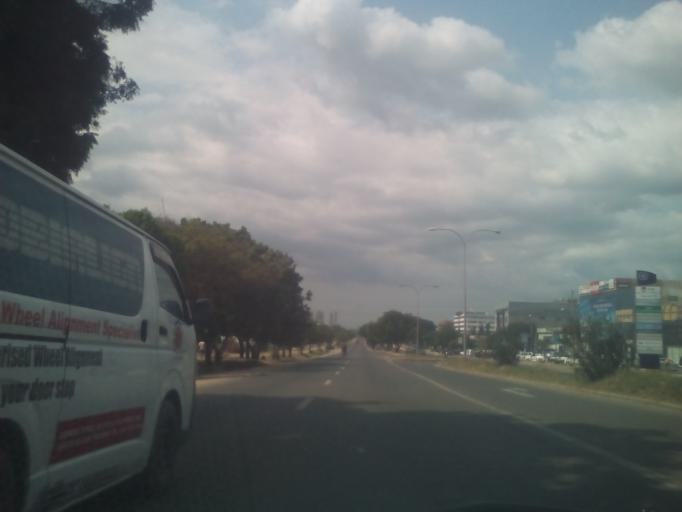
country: TZ
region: Dar es Salaam
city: Dar es Salaam
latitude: -6.8399
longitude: 39.2539
